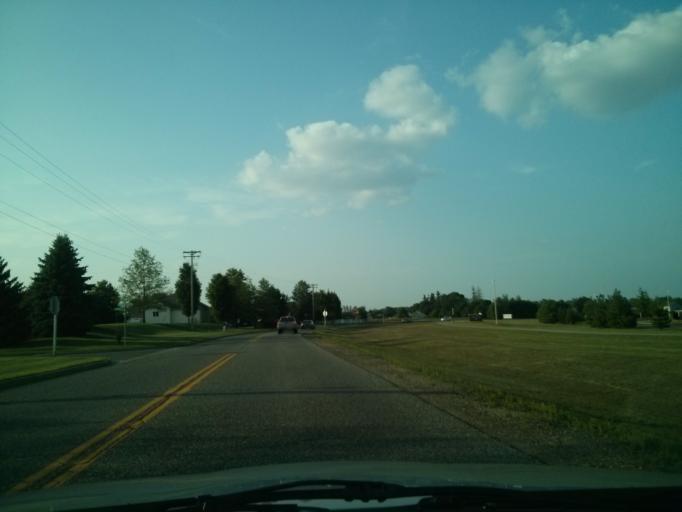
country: US
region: Wisconsin
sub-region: Saint Croix County
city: North Hudson
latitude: 44.9840
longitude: -92.7212
